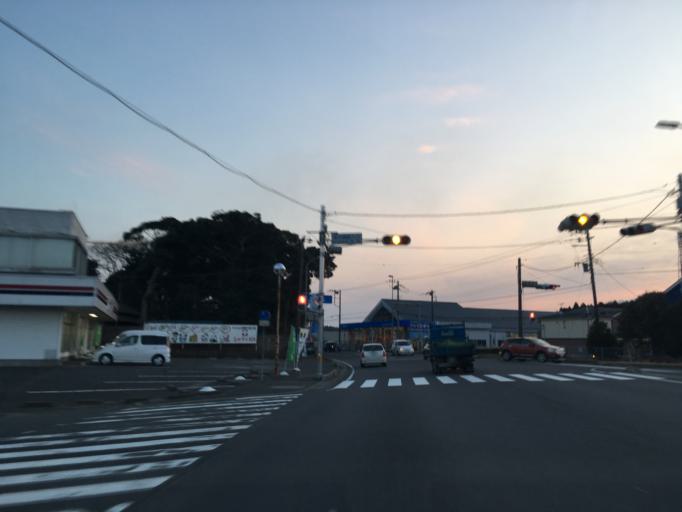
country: JP
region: Ibaraki
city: Kitaibaraki
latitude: 36.7525
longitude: 140.7321
